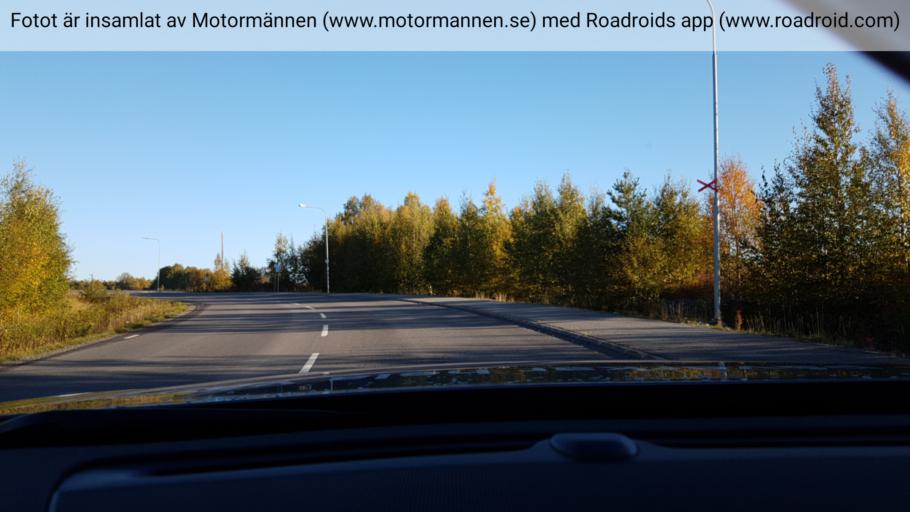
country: SE
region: Norrbotten
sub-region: Lulea Kommun
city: Sodra Sunderbyn
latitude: 65.6633
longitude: 21.9542
